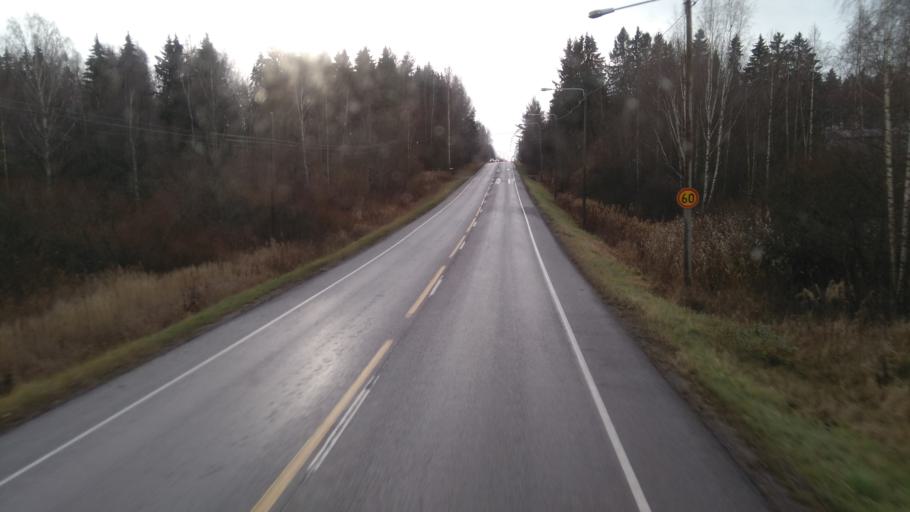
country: FI
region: Uusimaa
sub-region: Porvoo
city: Porvoo
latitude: 60.4070
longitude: 25.6930
